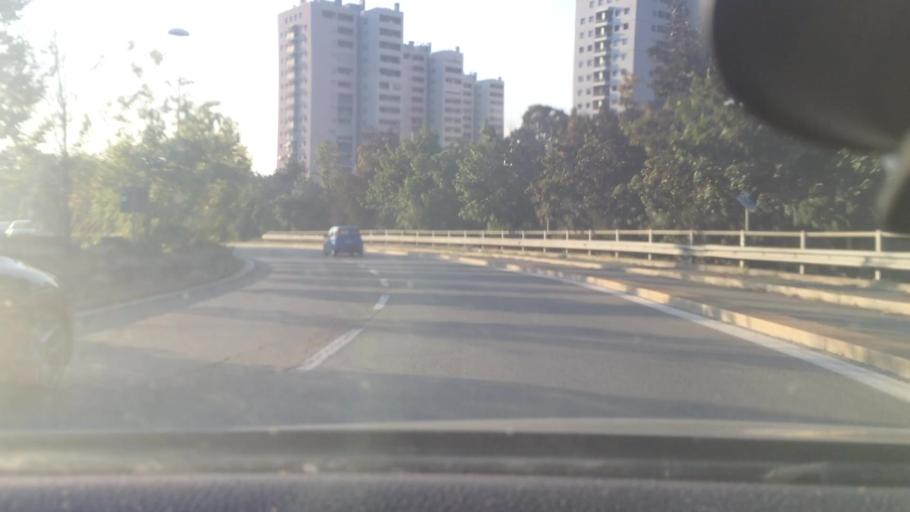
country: IT
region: Lombardy
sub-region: Citta metropolitana di Milano
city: Novate Milanese
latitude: 45.5067
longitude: 9.1406
